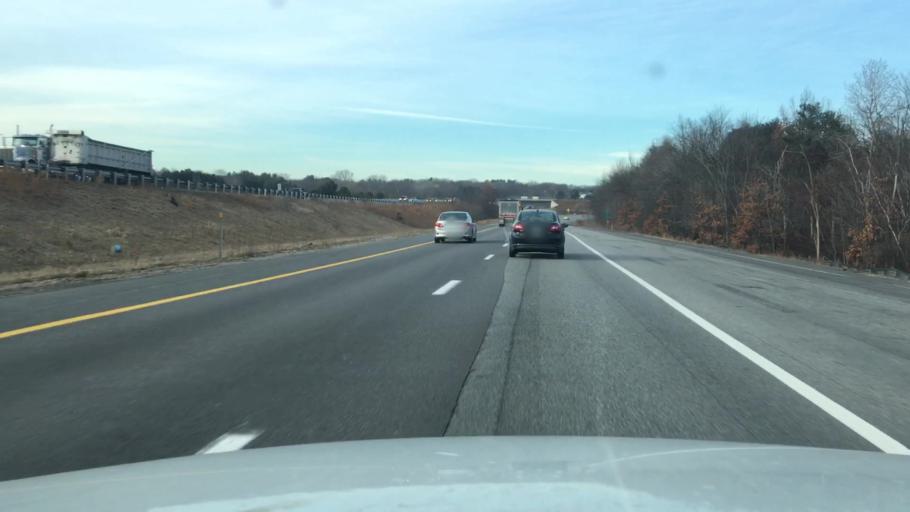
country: US
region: New Hampshire
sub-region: Hillsborough County
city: Manchester
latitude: 42.9632
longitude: -71.4103
